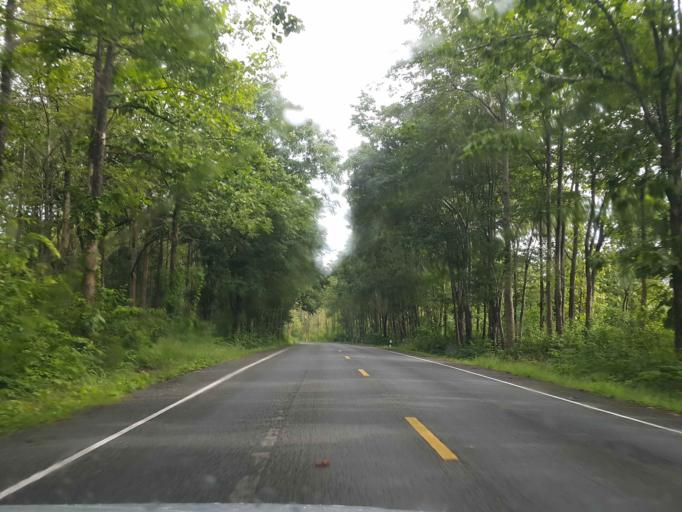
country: TH
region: Sukhothai
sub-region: Amphoe Si Satchanalai
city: Si Satchanalai
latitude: 17.6556
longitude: 99.7437
